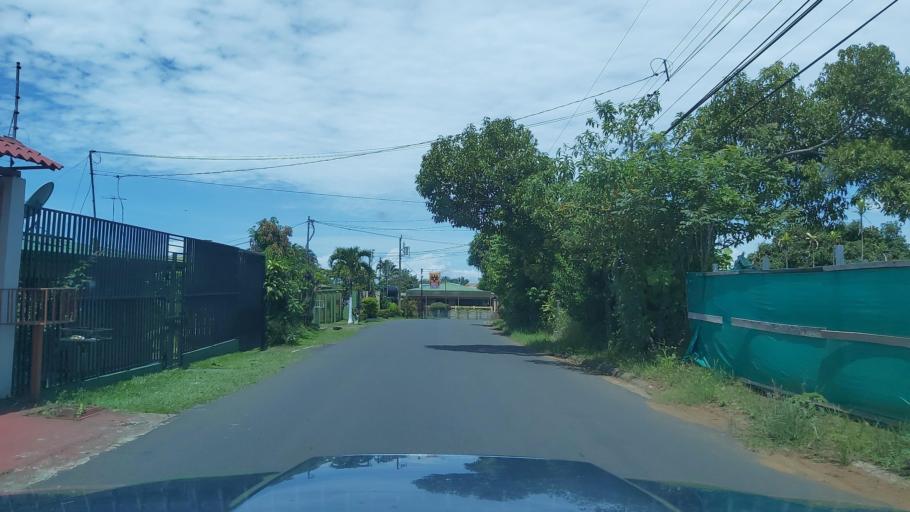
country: CR
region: Alajuela
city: San Juan
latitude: 10.0888
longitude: -84.3422
